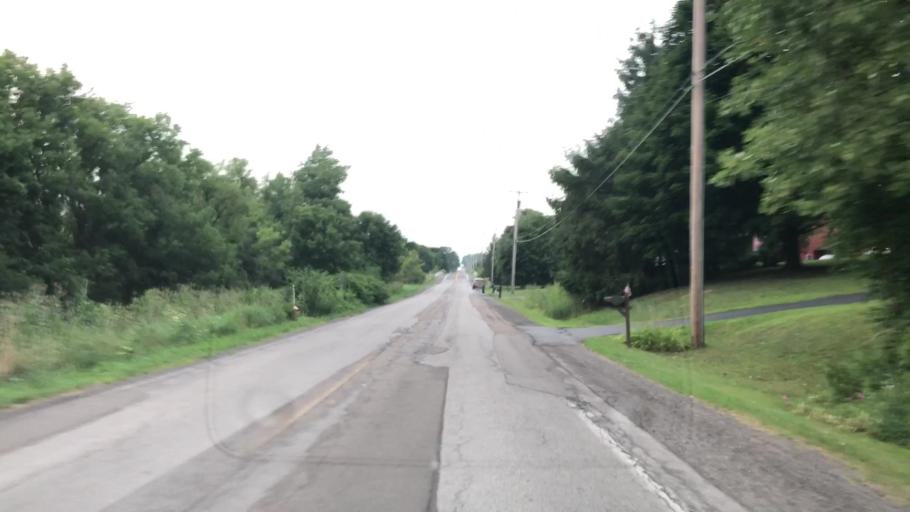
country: US
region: New York
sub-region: Erie County
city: Billington Heights
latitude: 42.7936
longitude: -78.6059
